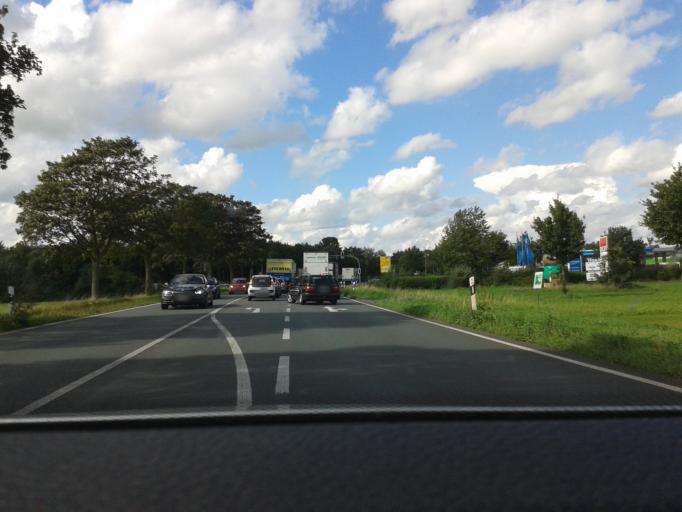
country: DE
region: North Rhine-Westphalia
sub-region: Regierungsbezirk Dusseldorf
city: Weeze
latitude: 51.6189
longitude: 6.2105
